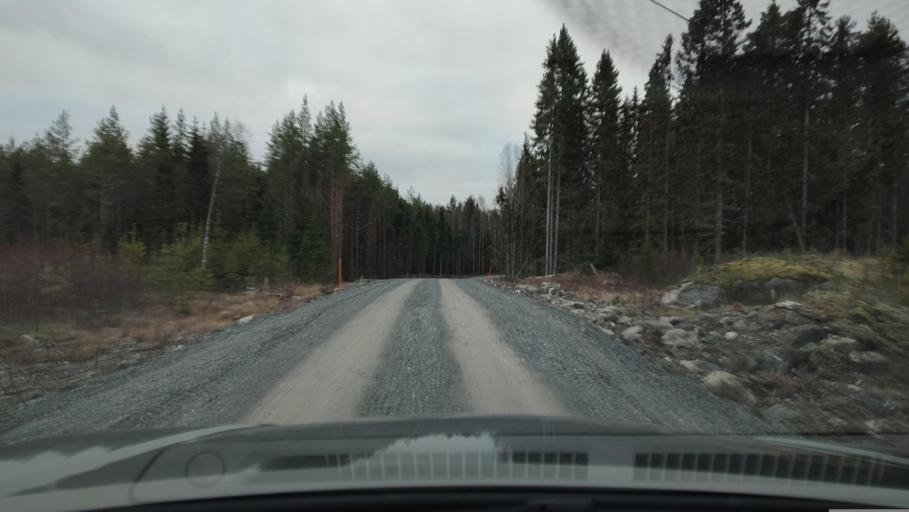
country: FI
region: Southern Ostrobothnia
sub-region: Suupohja
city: Karijoki
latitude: 62.1845
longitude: 21.5737
